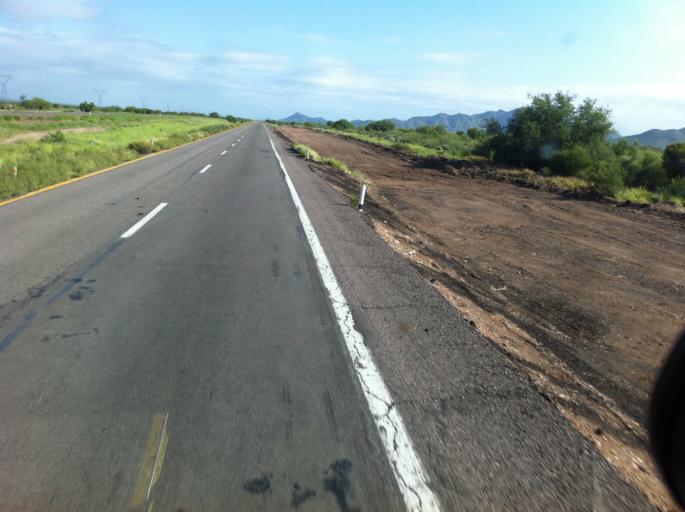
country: MX
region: Sonora
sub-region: Hermosillo
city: Miguel Aleman (La Doce)
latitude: 28.5402
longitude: -111.0425
